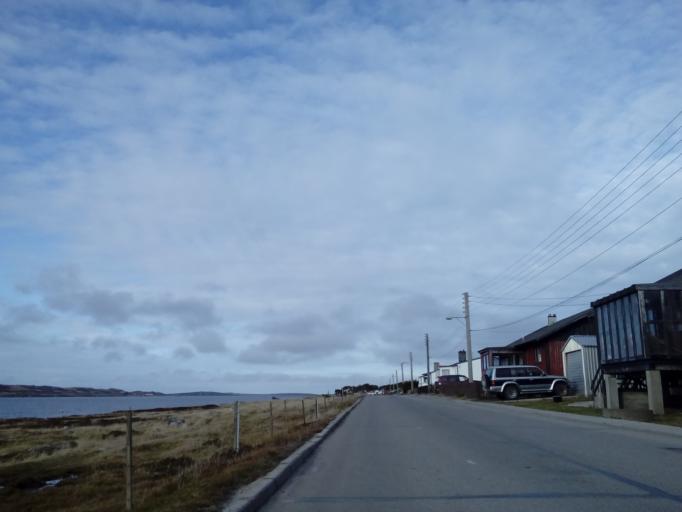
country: FK
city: Stanley
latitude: -51.6899
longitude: -57.8907
